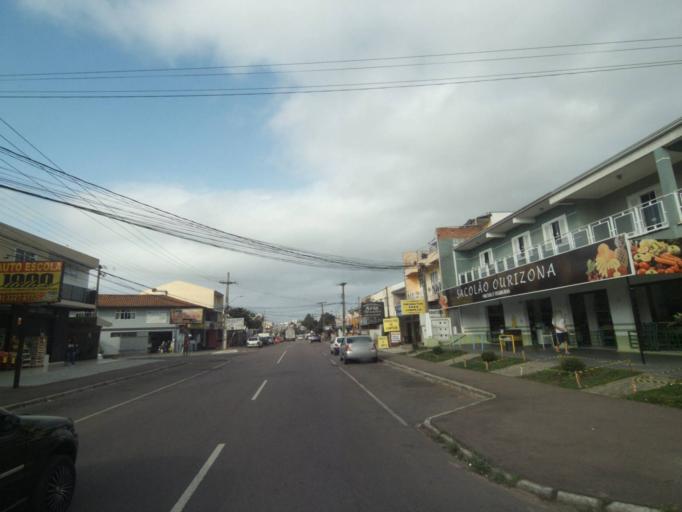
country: BR
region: Parana
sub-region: Sao Jose Dos Pinhais
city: Sao Jose dos Pinhais
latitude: -25.5398
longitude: -49.2565
